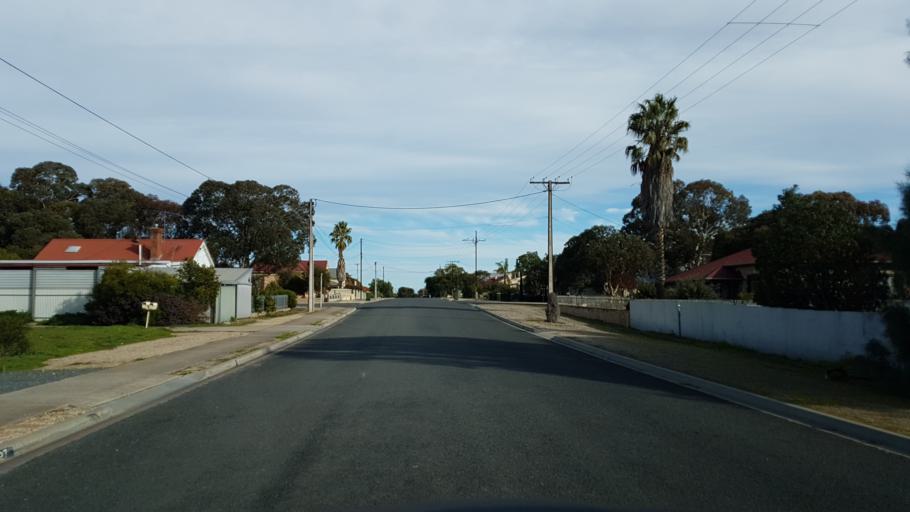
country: AU
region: South Australia
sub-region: Murray Bridge
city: Tailem Bend
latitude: -35.2517
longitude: 139.4601
